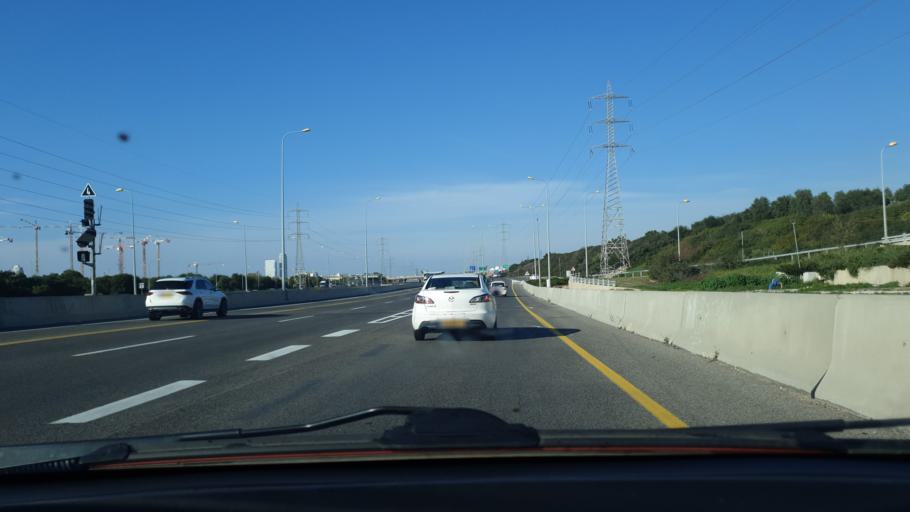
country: IL
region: Central District
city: Rishon LeZiyyon
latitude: 31.9798
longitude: 34.7563
